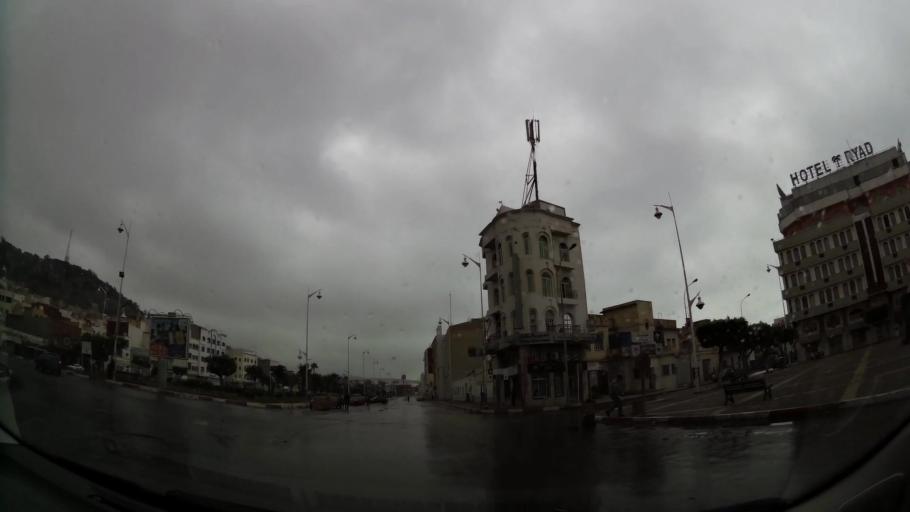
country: MA
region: Oriental
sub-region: Nador
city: Nador
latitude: 35.1793
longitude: -2.9279
